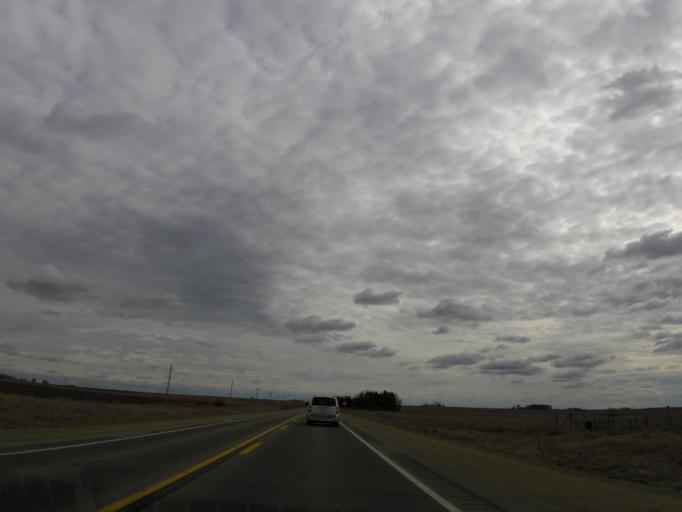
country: US
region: Iowa
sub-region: Chickasaw County
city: New Hampton
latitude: 43.1584
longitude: -92.2989
